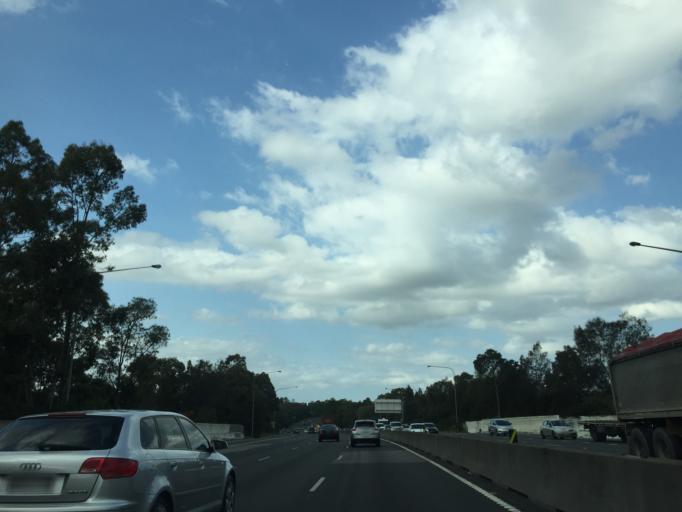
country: AU
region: New South Wales
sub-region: Holroyd
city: Merrylands
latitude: -33.8171
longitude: 150.9682
